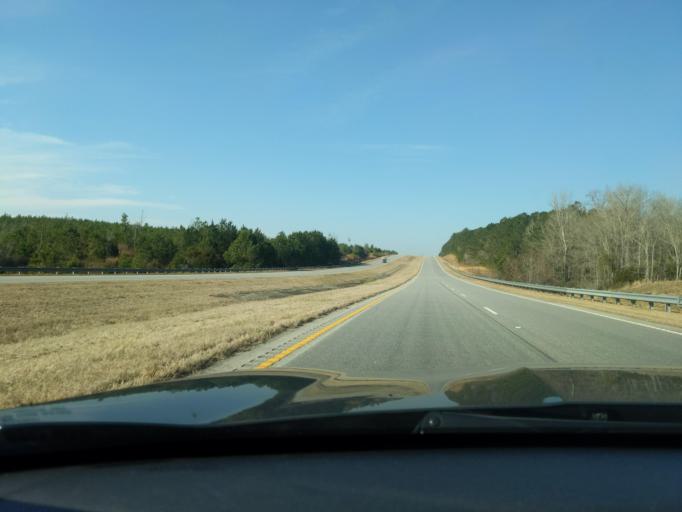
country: US
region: South Carolina
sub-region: Abbeville County
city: Calhoun Falls
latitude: 34.1132
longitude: -82.4821
